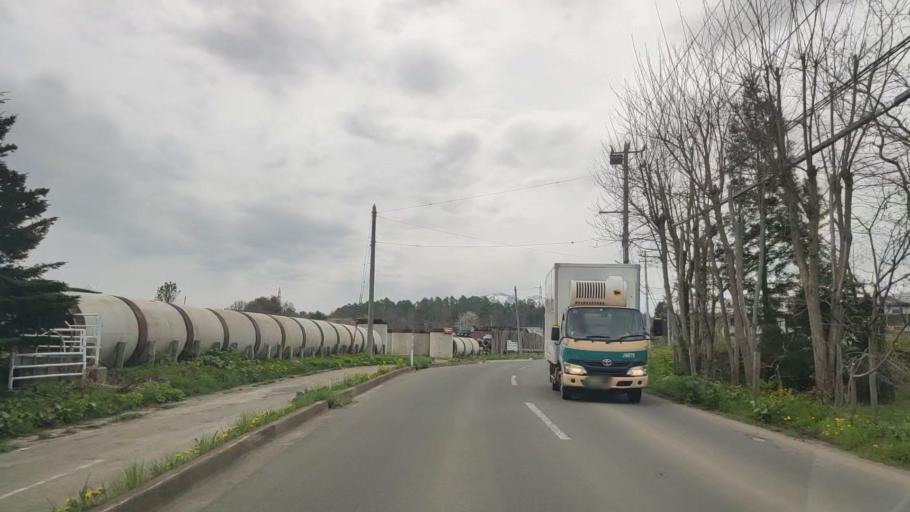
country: JP
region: Aomori
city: Aomori Shi
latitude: 40.7722
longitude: 140.7980
